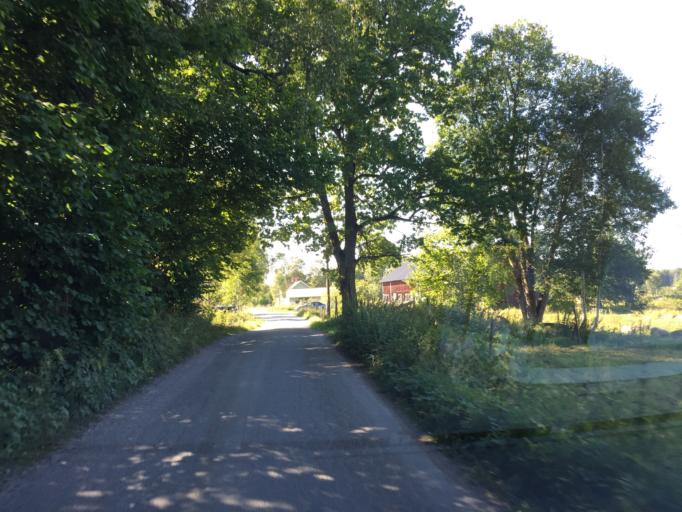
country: SE
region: OEstergoetland
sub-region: Finspangs Kommun
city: Finspang
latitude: 58.8928
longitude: 15.7005
